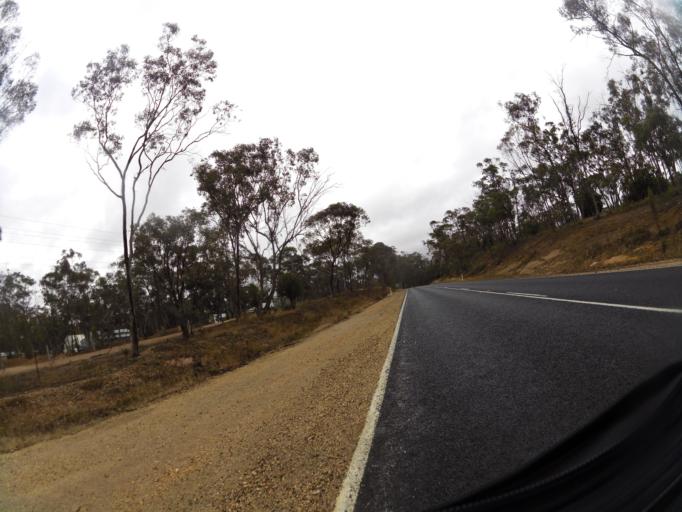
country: AU
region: Victoria
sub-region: Mount Alexander
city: Castlemaine
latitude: -37.0709
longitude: 144.1720
